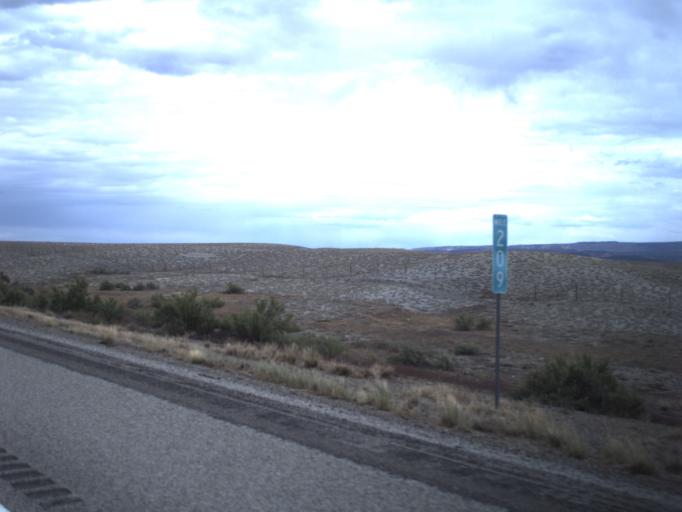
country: US
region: Utah
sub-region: Grand County
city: Moab
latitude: 38.9779
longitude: -109.3477
